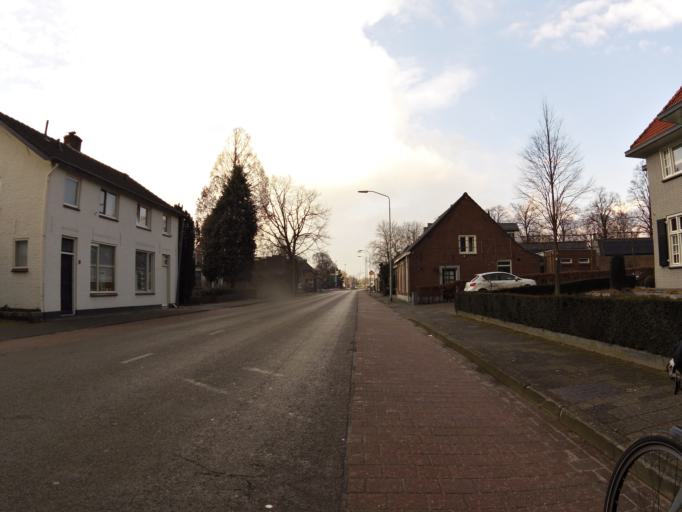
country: NL
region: North Brabant
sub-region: Gemeente Boxtel
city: Boxtel
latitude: 51.5950
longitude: 5.3246
